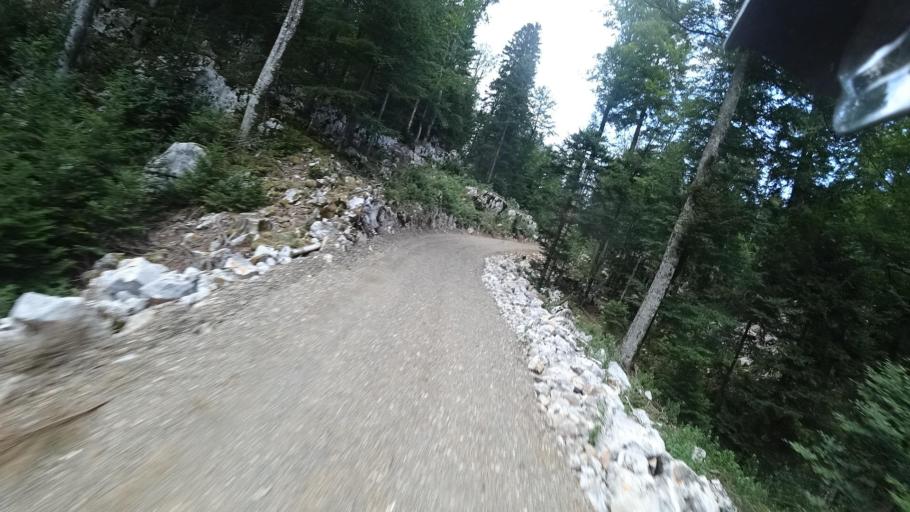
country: HR
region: Licko-Senjska
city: Senj
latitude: 45.1331
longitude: 14.9725
